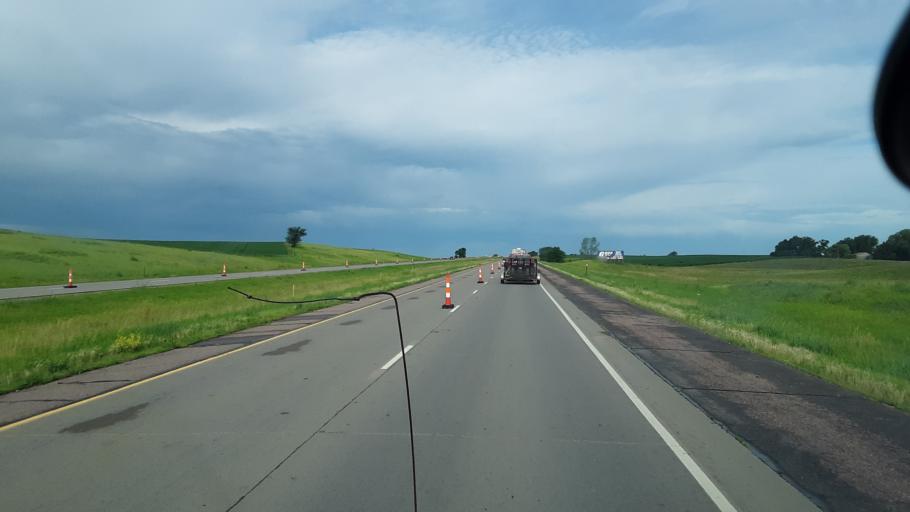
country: US
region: South Dakota
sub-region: Minnehaha County
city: Crooks
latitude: 43.6087
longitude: -96.8430
